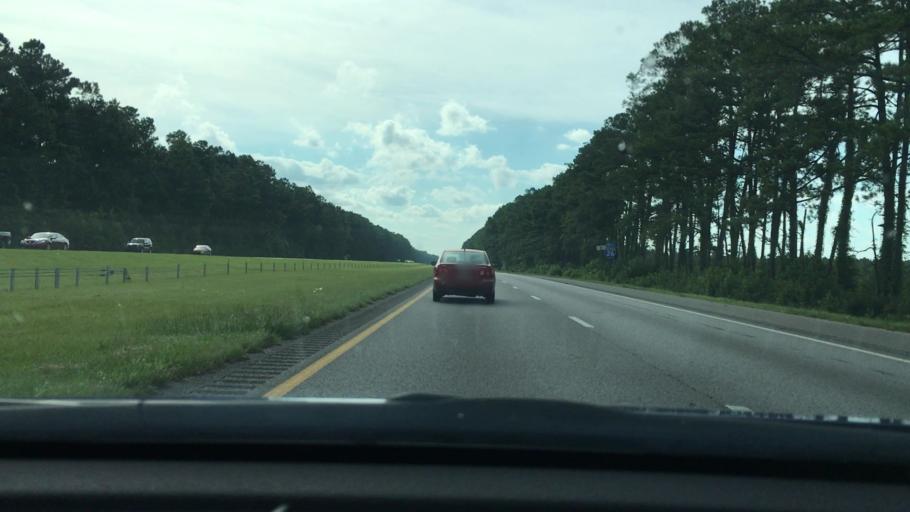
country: US
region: South Carolina
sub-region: Dorchester County
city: Summerville
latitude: 33.0849
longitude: -80.2124
